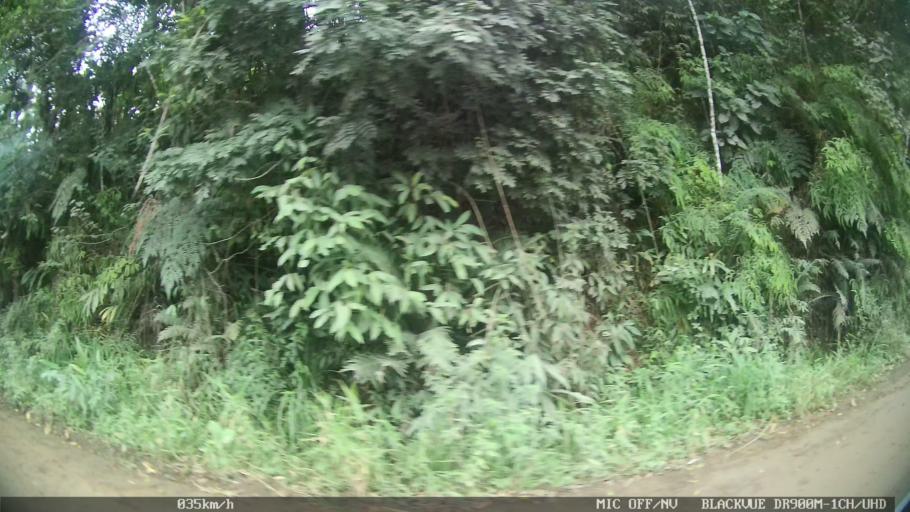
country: BR
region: Santa Catarina
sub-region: Joinville
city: Joinville
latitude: -26.2486
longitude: -48.9252
